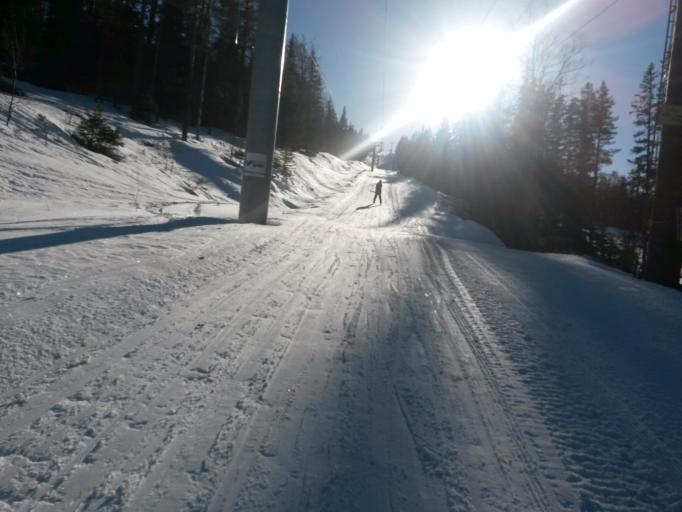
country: SE
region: Vaesterbotten
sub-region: Skelleftea Kommun
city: Langsele
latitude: 65.1579
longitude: 20.1334
